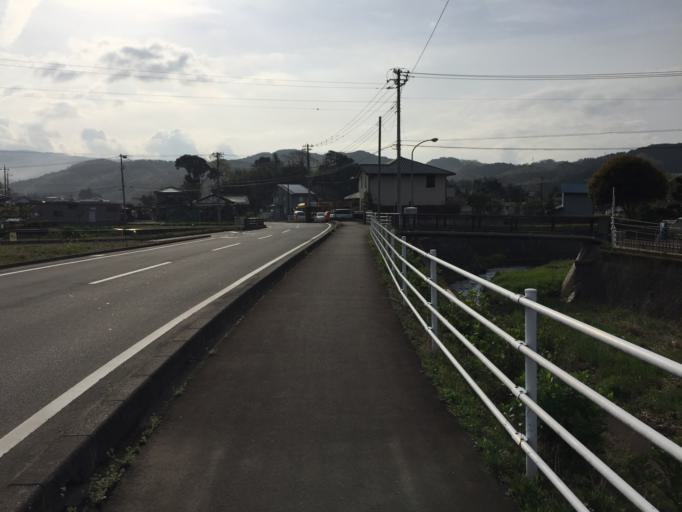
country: JP
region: Shizuoka
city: Mishima
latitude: 35.1714
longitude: 138.9216
